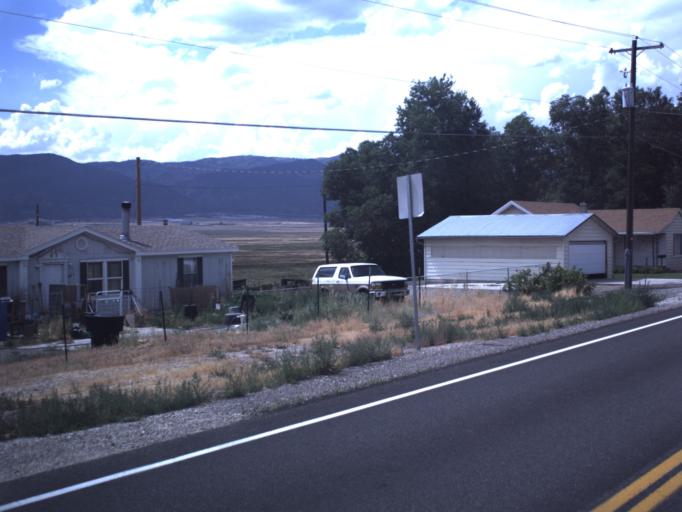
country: US
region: Utah
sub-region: Sanpete County
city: Moroni
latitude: 39.5327
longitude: -111.5914
